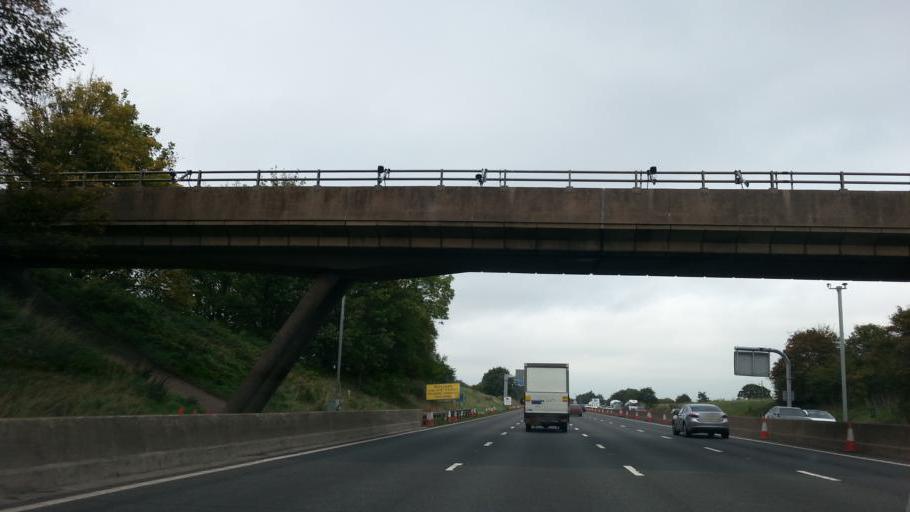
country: GB
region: England
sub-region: Staffordshire
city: Penkridge
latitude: 52.7426
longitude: -2.0994
